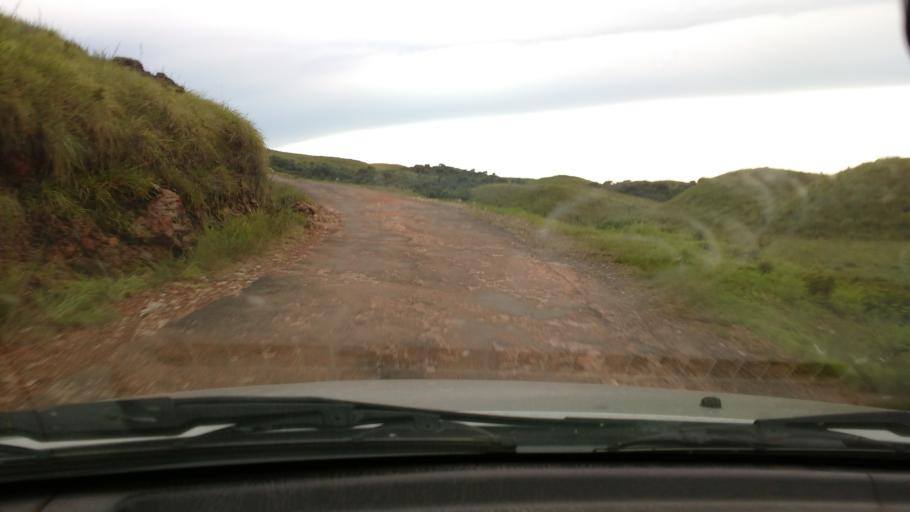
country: IN
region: Meghalaya
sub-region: East Khasi Hills
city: Cherrapunji
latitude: 25.2797
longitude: 91.6962
